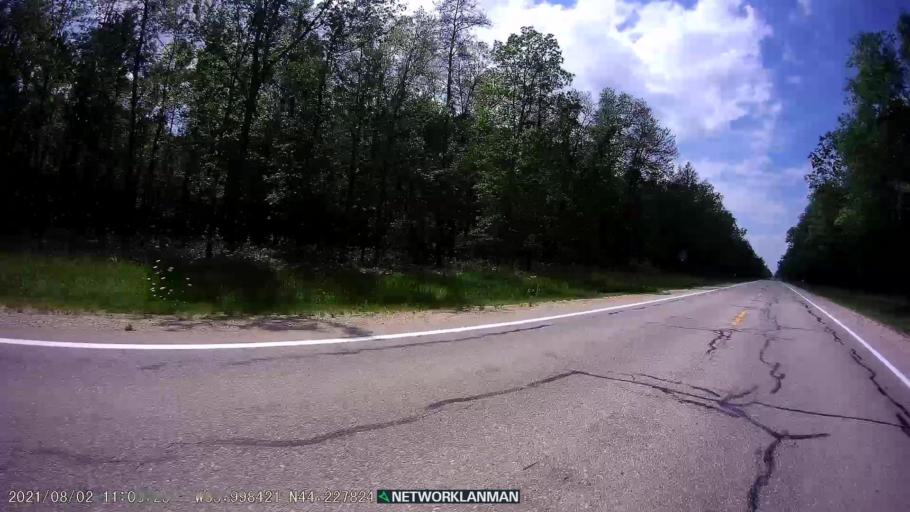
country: US
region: Michigan
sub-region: Manistee County
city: Manistee
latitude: 44.2279
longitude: -85.9989
